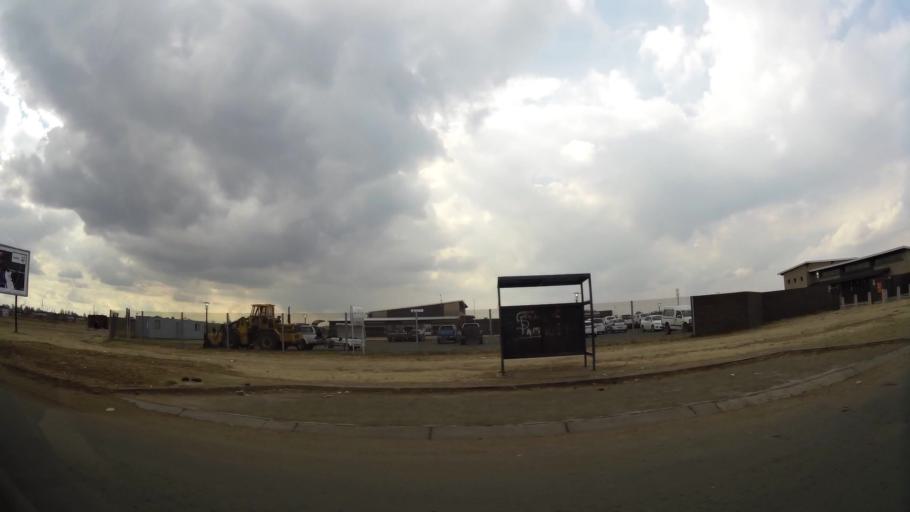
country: ZA
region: Orange Free State
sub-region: Fezile Dabi District Municipality
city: Sasolburg
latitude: -26.8555
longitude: 27.8820
